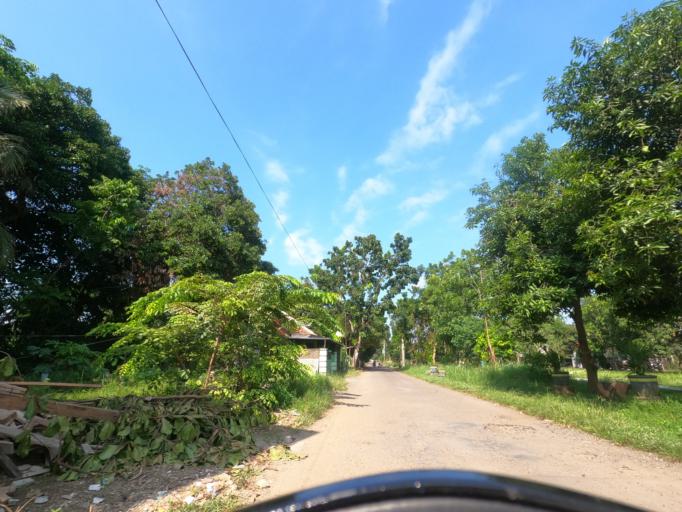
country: ID
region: West Java
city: Lembang
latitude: -6.5797
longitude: 107.7804
